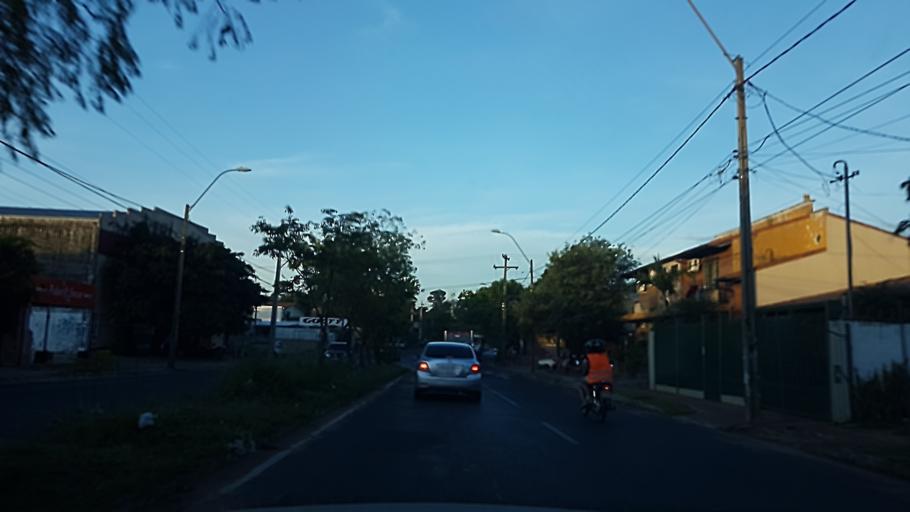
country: PY
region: Asuncion
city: Asuncion
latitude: -25.2565
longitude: -57.5780
